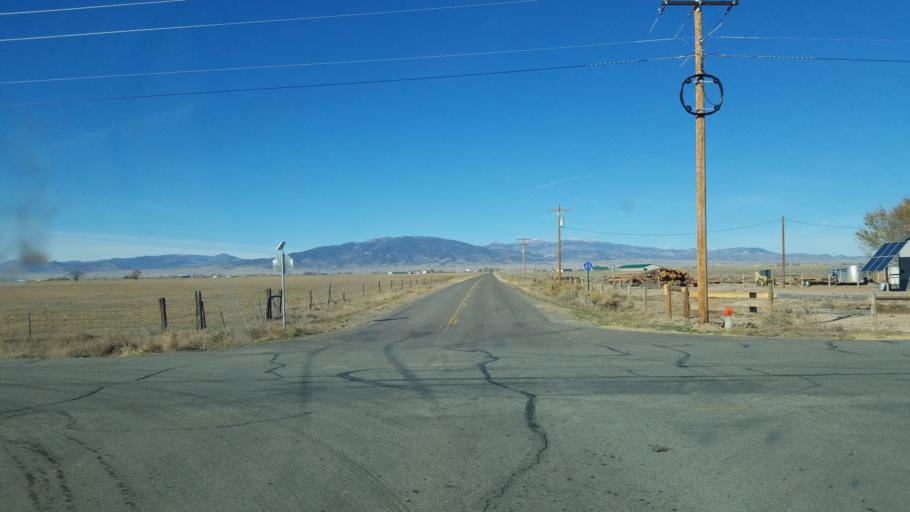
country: US
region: Colorado
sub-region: Rio Grande County
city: Monte Vista
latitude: 37.4588
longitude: -106.0392
